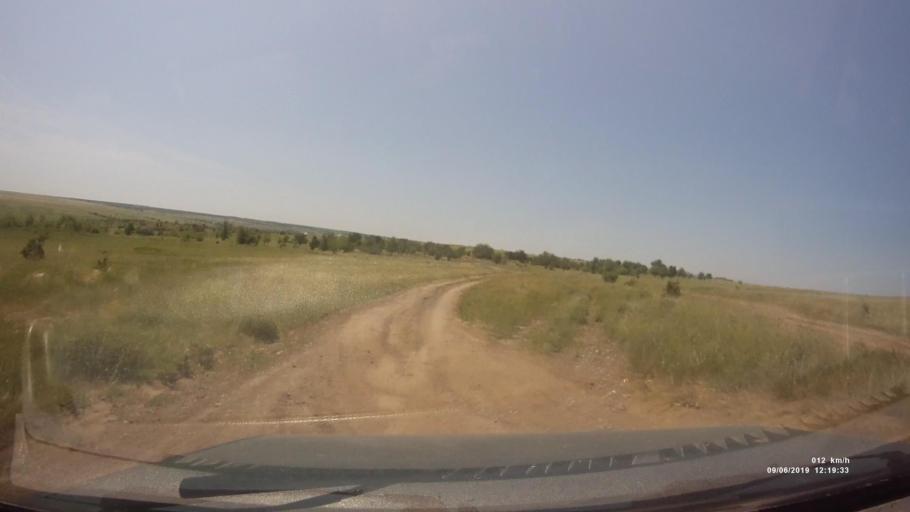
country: RU
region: Rostov
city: Kamensk-Shakhtinskiy
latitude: 48.2534
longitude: 40.3061
